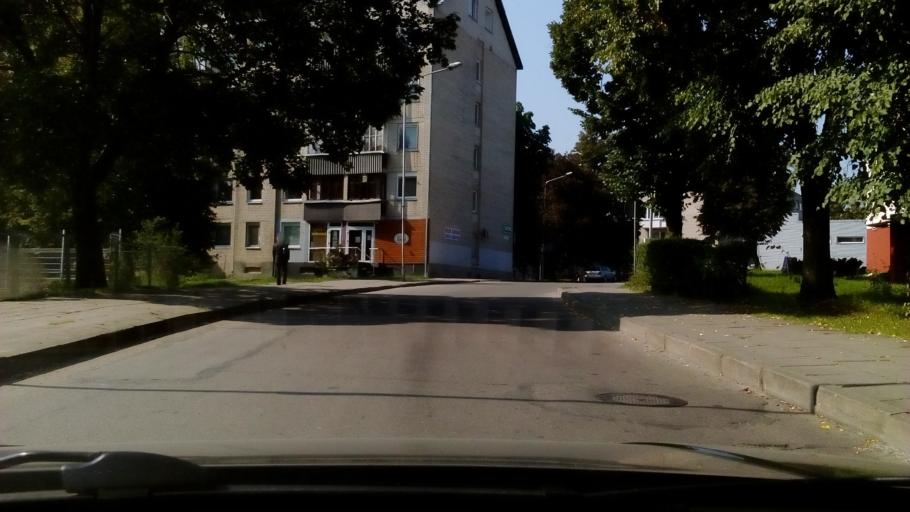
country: LT
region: Alytaus apskritis
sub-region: Alytus
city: Alytus
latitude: 54.3978
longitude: 24.0350
